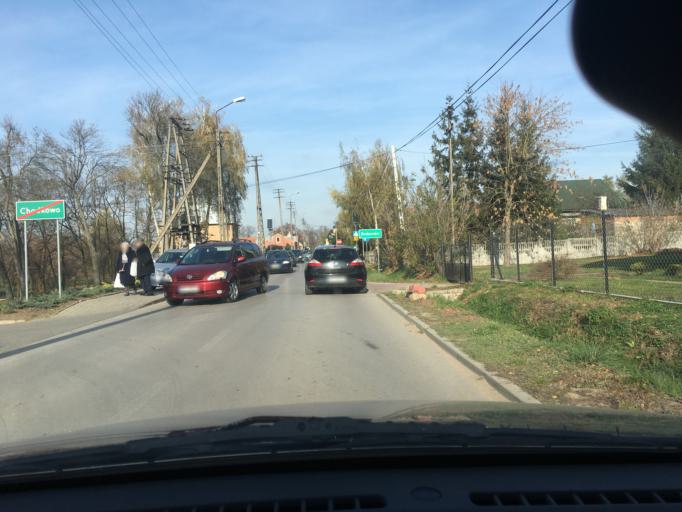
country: PL
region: Masovian Voivodeship
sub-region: Powiat plocki
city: Bodzanow
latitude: 52.4979
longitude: 20.0302
